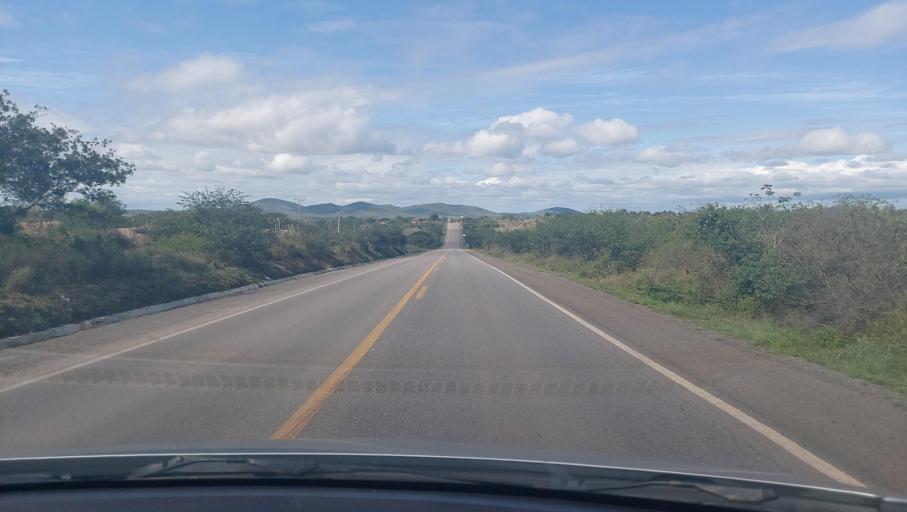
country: BR
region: Bahia
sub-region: Ipira
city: Ipira
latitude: -12.4811
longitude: -39.7520
